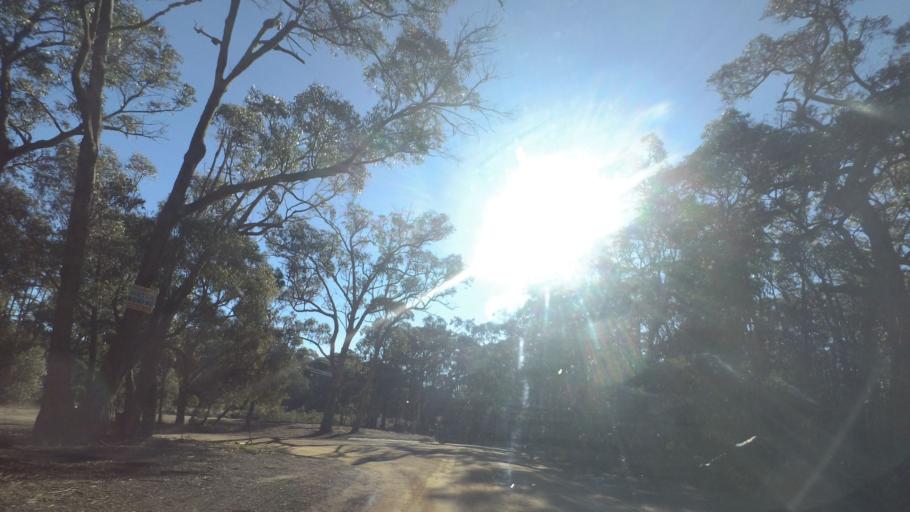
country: AU
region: Victoria
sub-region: Moorabool
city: Bacchus Marsh
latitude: -37.3917
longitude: 144.4882
